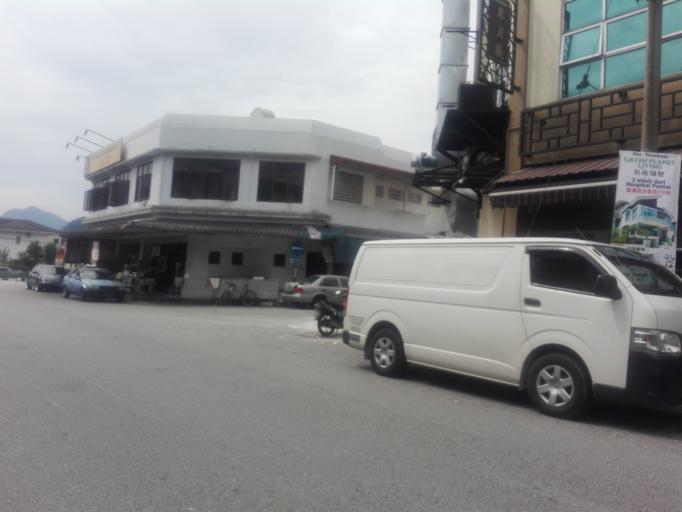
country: MY
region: Perak
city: Ipoh
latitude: 4.6082
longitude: 101.1196
